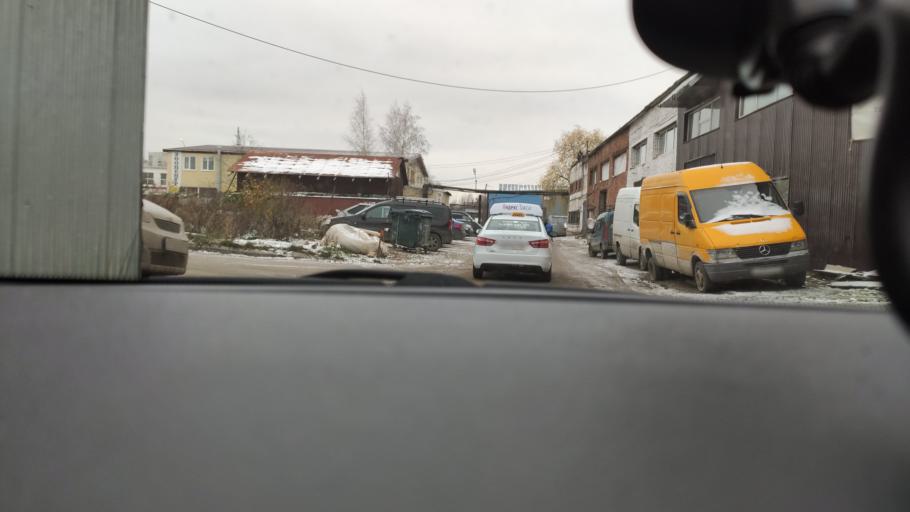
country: RU
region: Perm
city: Perm
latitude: 57.9856
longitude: 56.2747
